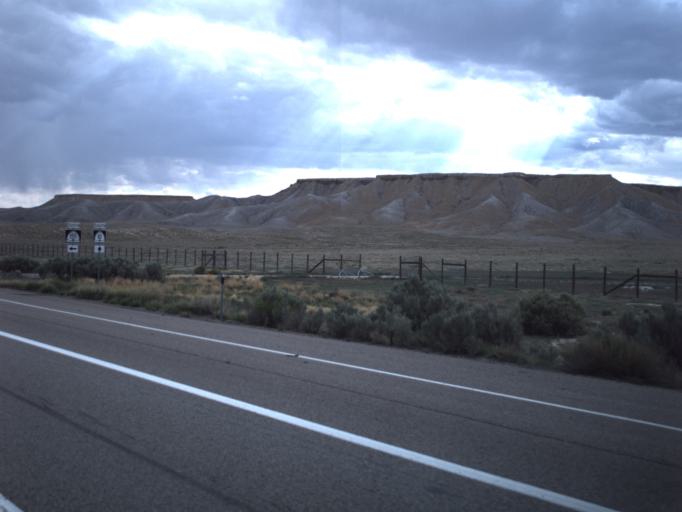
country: US
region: Utah
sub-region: Emery County
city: Huntington
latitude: 39.4337
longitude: -110.8675
